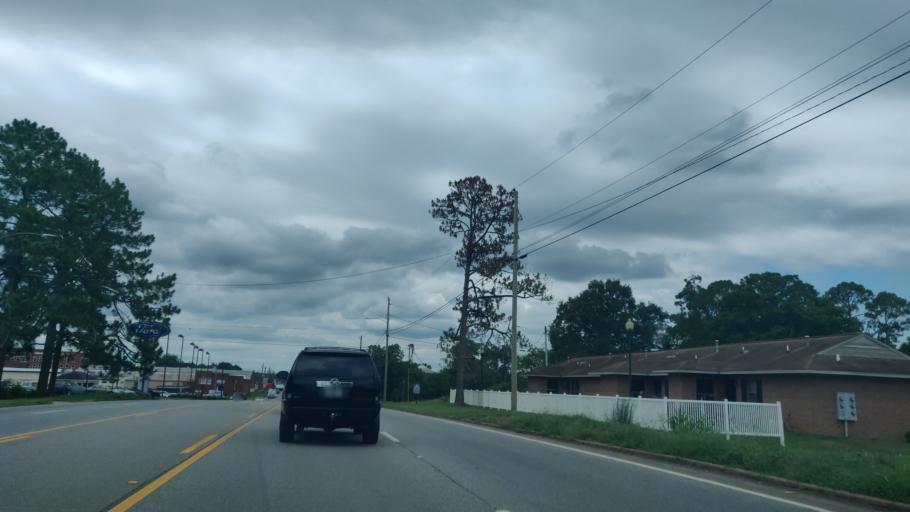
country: US
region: Georgia
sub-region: Terrell County
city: Dawson
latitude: 31.7764
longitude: -84.4481
